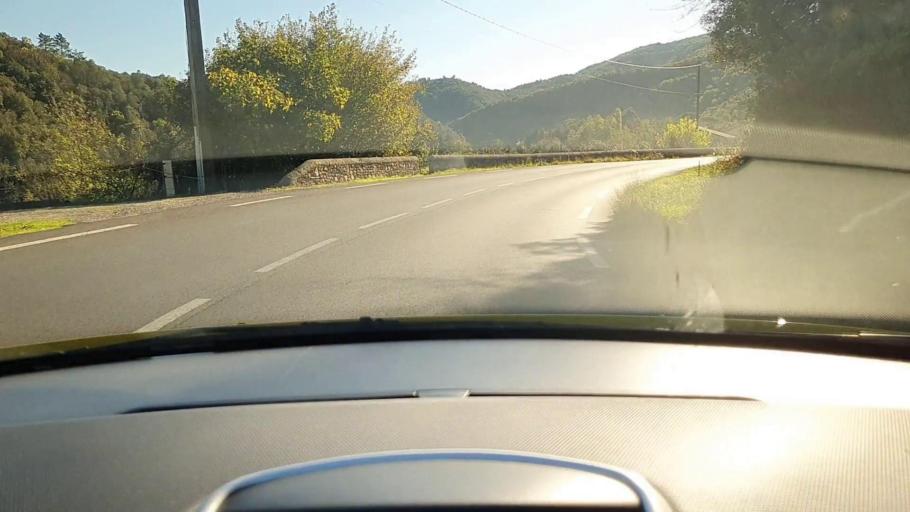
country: FR
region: Languedoc-Roussillon
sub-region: Departement du Gard
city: Sumene
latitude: 44.0027
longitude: 3.6766
